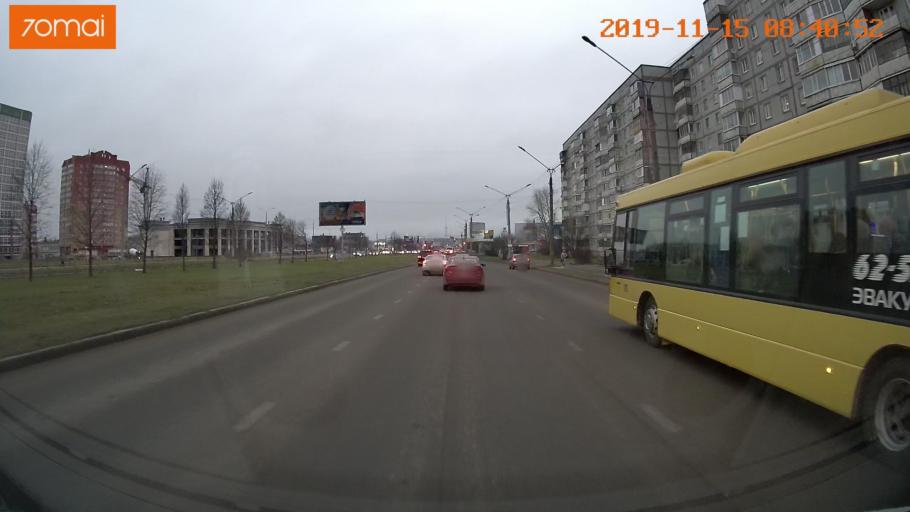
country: RU
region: Vologda
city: Cherepovets
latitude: 59.0962
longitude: 37.9129
